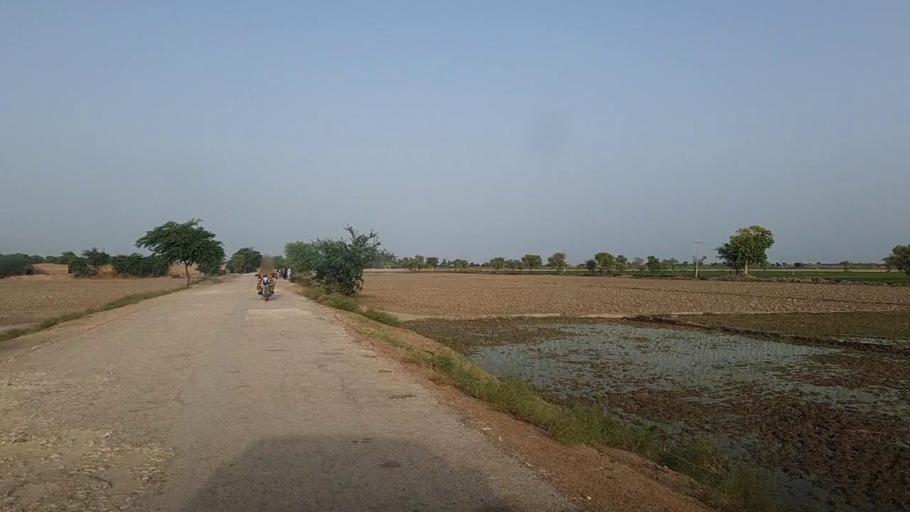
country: PK
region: Sindh
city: Mehar
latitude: 27.1639
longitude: 67.7870
